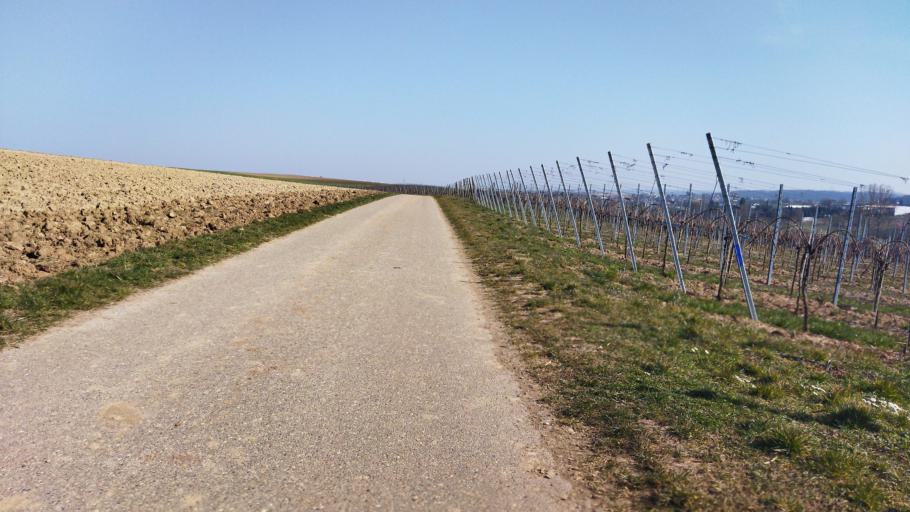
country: DE
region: Baden-Wuerttemberg
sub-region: Regierungsbezirk Stuttgart
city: Brackenheim
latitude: 49.0875
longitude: 9.0847
